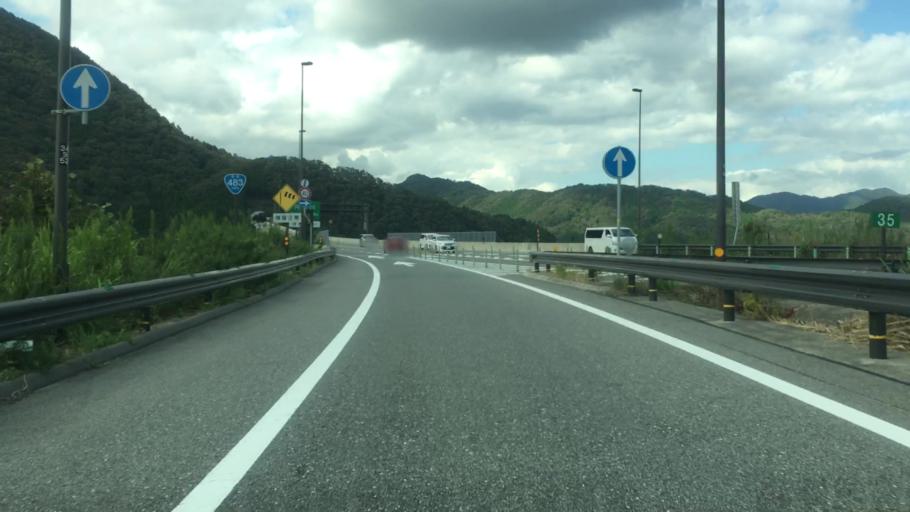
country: JP
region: Hyogo
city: Toyooka
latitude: 35.3161
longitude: 134.8460
